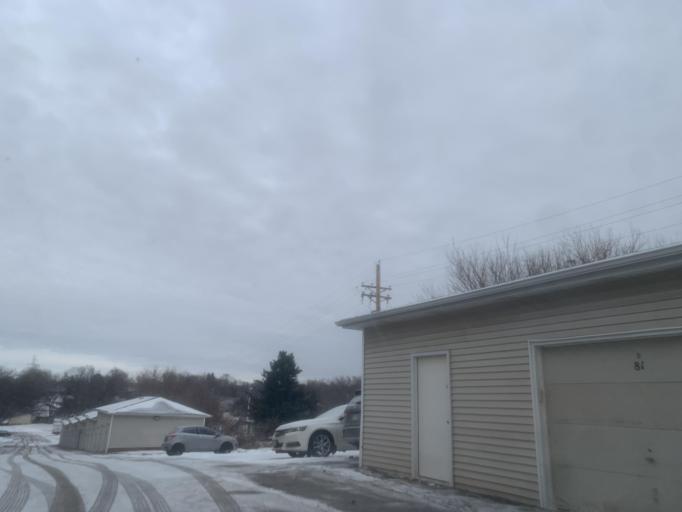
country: US
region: Nebraska
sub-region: Douglas County
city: Ralston
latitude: 41.2712
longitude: -96.0794
